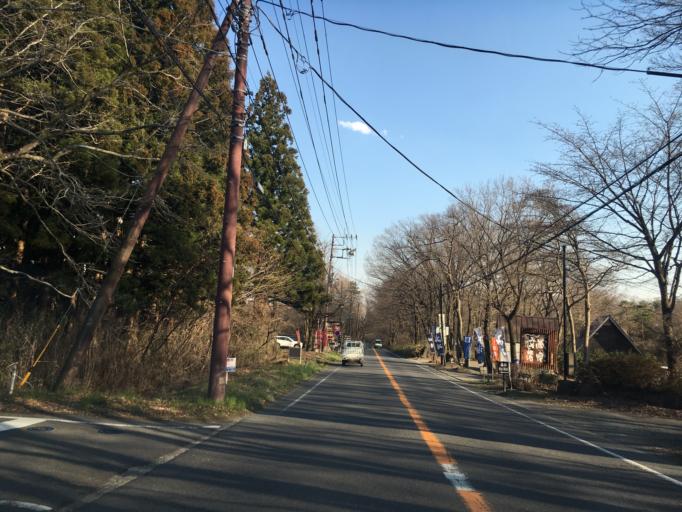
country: JP
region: Tochigi
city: Kuroiso
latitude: 37.0377
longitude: 140.0170
